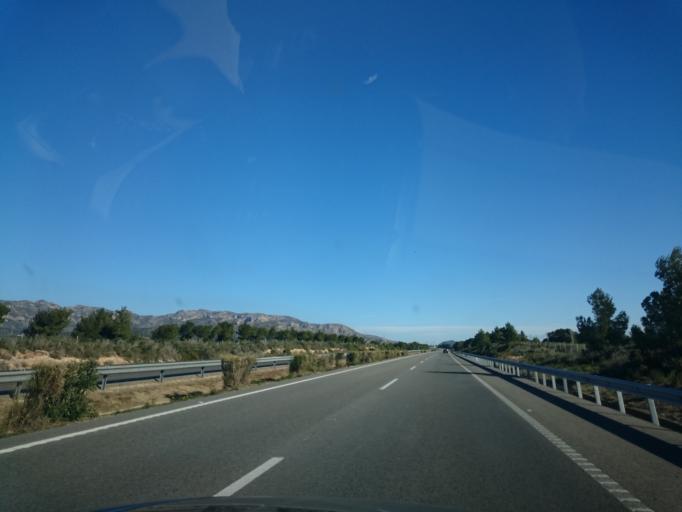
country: ES
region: Catalonia
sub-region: Provincia de Tarragona
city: l'Ametlla de Mar
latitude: 40.9192
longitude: 0.8314
